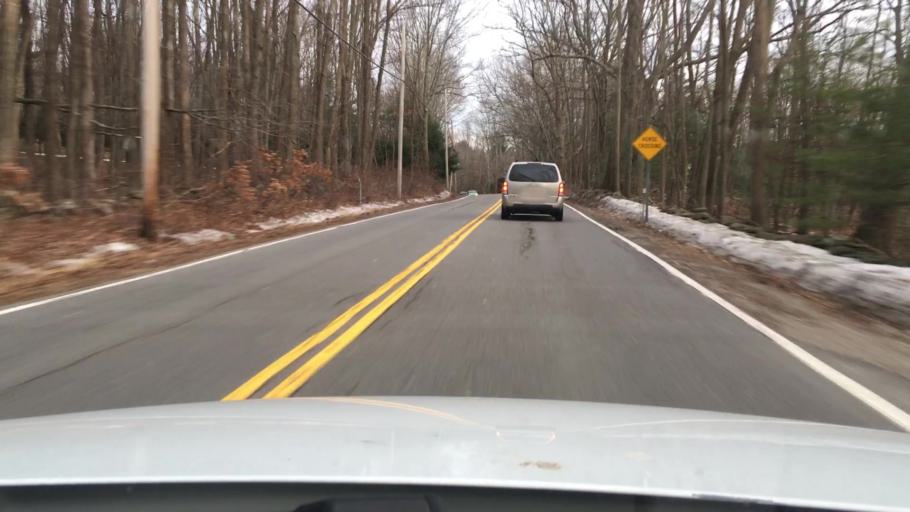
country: US
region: New Hampshire
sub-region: Rockingham County
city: Atkinson
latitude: 42.8266
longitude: -71.1359
